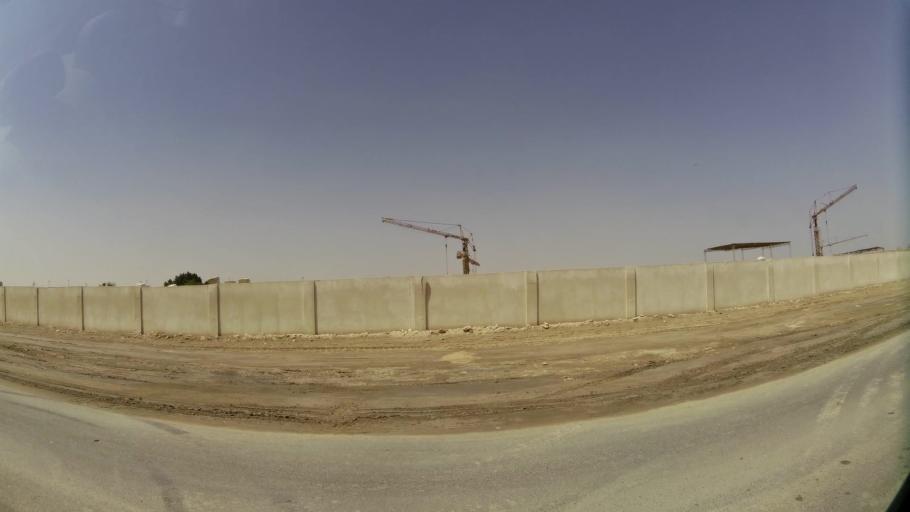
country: QA
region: Baladiyat Umm Salal
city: Umm Salal Muhammad
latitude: 25.3787
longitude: 51.4481
